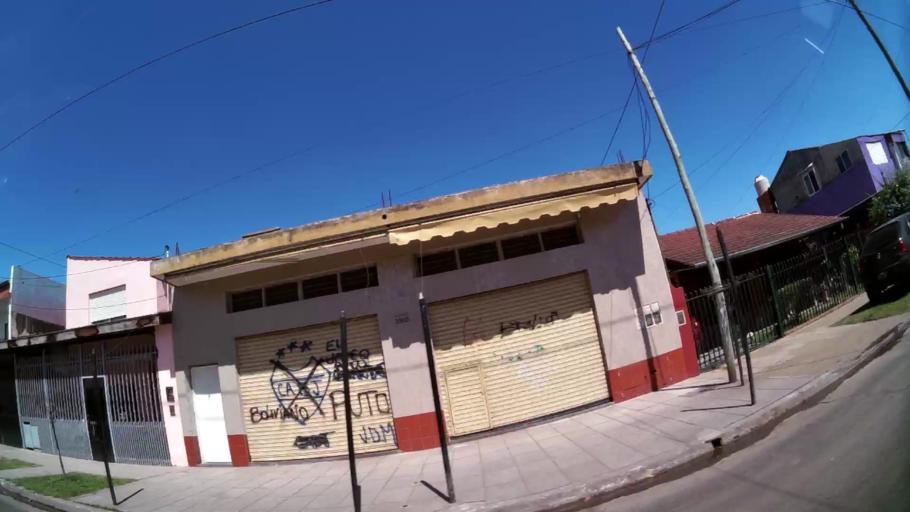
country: AR
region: Buenos Aires
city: Hurlingham
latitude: -34.5076
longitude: -58.6717
